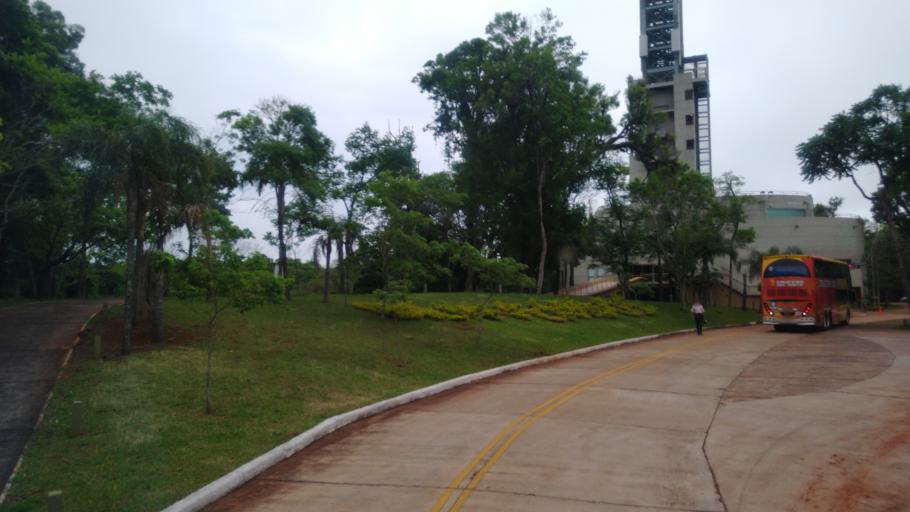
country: AR
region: Misiones
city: Cerro Cora
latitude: -27.4491
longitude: -55.5753
